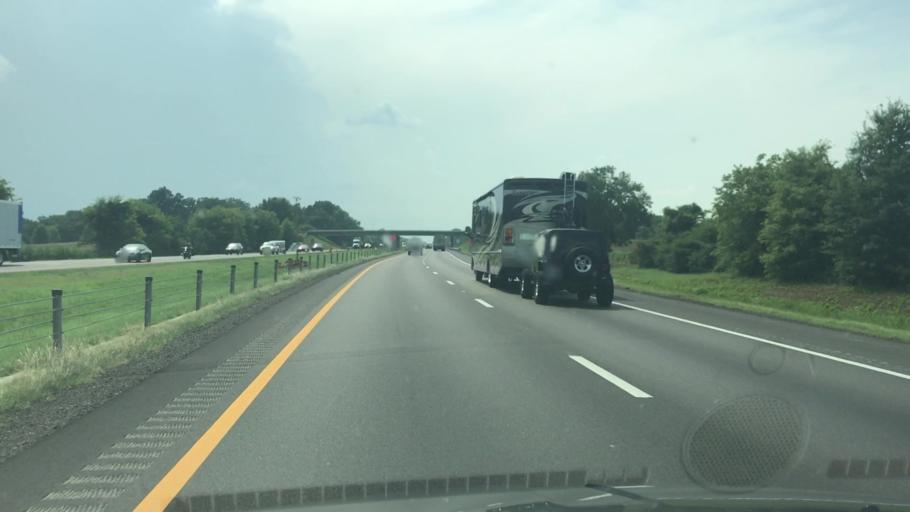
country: US
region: Arkansas
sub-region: Crittenden County
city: Earle
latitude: 35.1343
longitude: -90.4409
